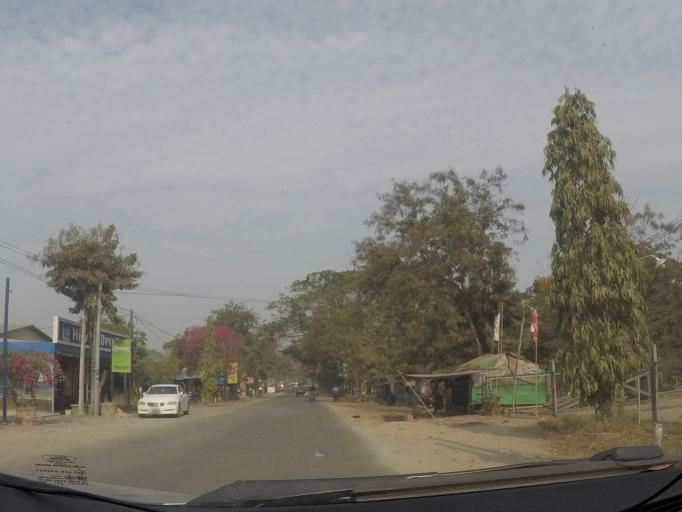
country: MM
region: Bago
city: Pyay
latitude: 18.8045
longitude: 95.2374
